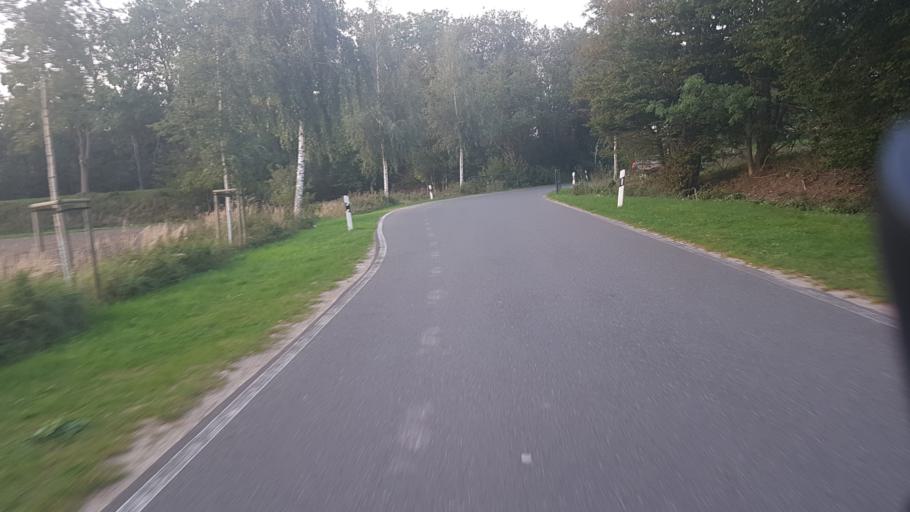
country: DE
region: Mecklenburg-Vorpommern
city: Ostseebad Binz
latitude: 54.3678
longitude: 13.6281
